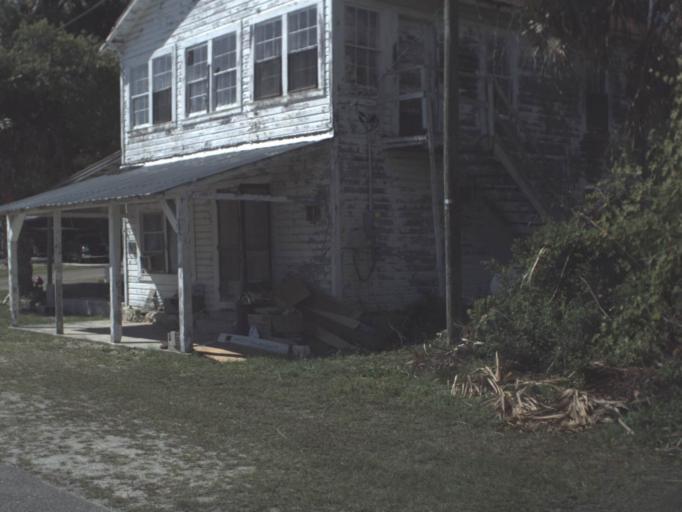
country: US
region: Florida
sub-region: Taylor County
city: Steinhatchee
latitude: 29.6703
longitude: -83.3859
